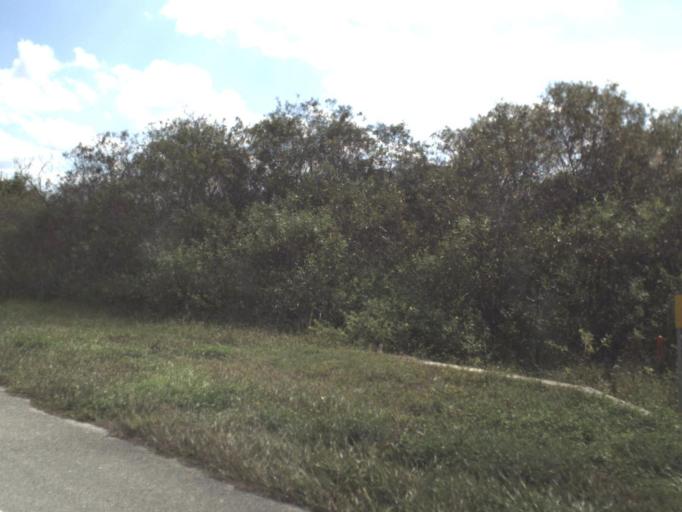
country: US
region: Florida
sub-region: Highlands County
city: Lake Placid
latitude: 27.4208
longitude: -81.2057
